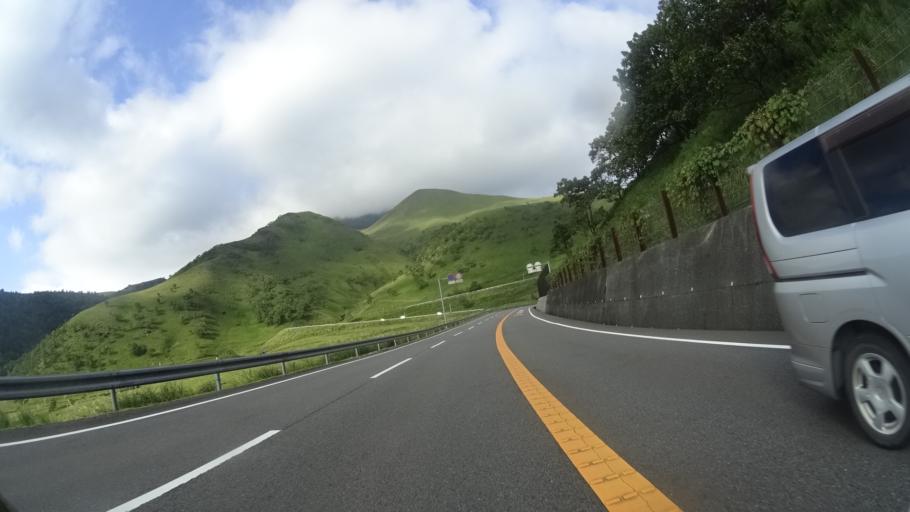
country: JP
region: Oita
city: Beppu
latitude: 33.2612
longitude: 131.3817
